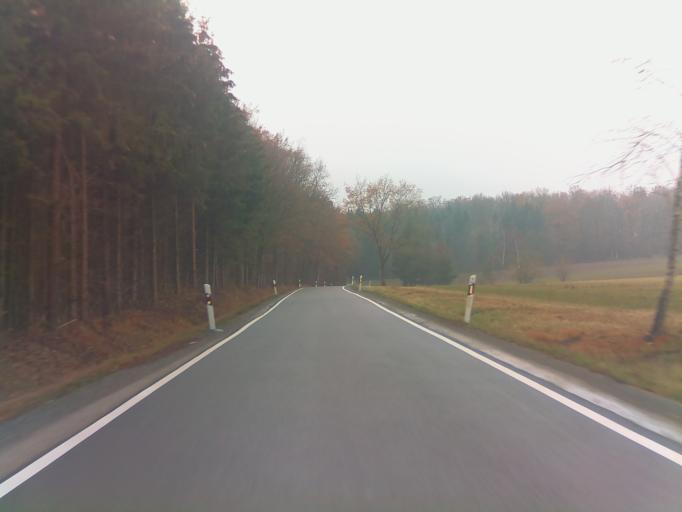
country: DE
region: Bavaria
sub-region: Regierungsbezirk Unterfranken
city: Hochheim
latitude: 50.4025
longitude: 10.4559
